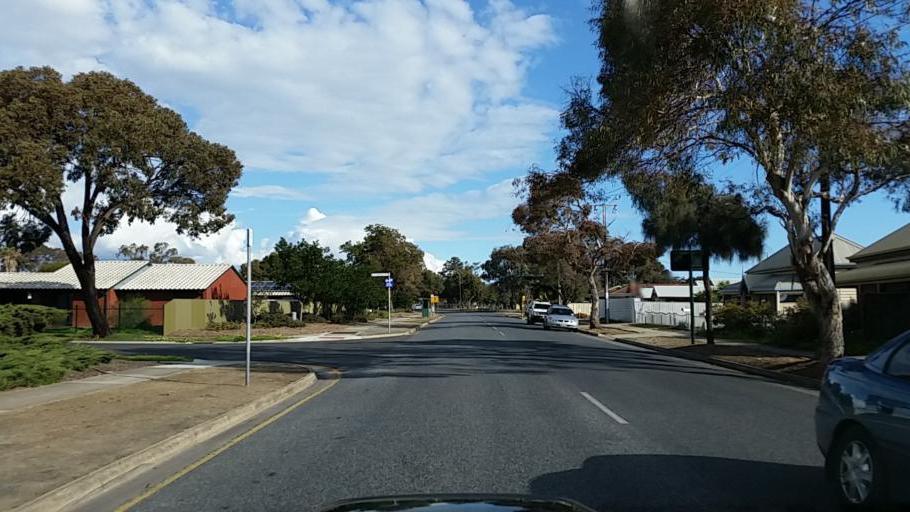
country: AU
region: South Australia
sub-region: Charles Sturt
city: West Lakes Shore
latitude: -34.8524
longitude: 138.4930
